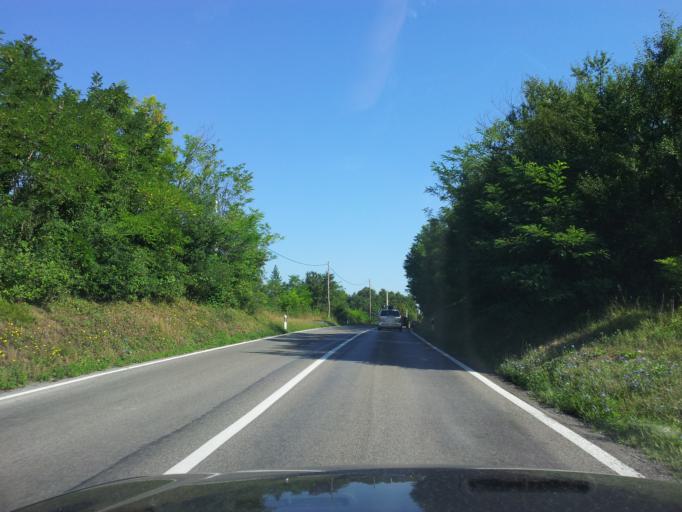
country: HR
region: Karlovacka
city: Vojnic
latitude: 45.2646
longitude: 15.5569
